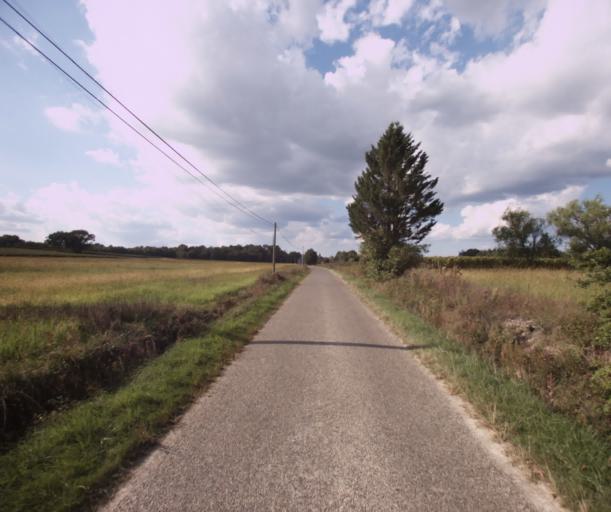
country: FR
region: Midi-Pyrenees
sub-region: Departement du Gers
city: Cazaubon
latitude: 43.8912
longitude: -0.0417
